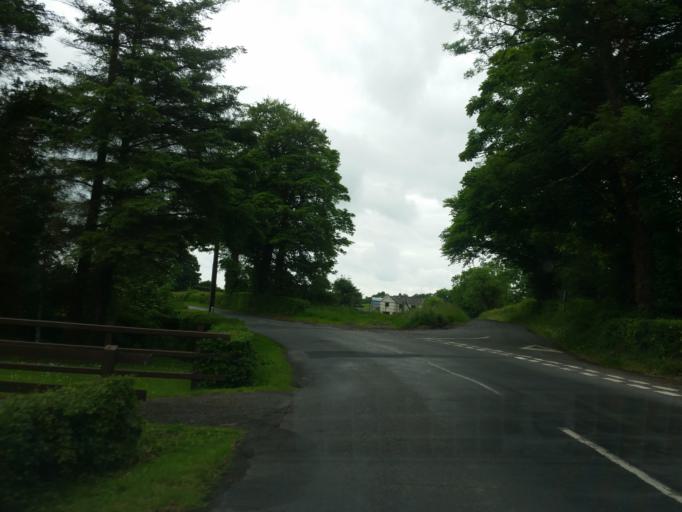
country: GB
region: Northern Ireland
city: Lisnaskea
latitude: 54.3104
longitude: -7.4124
